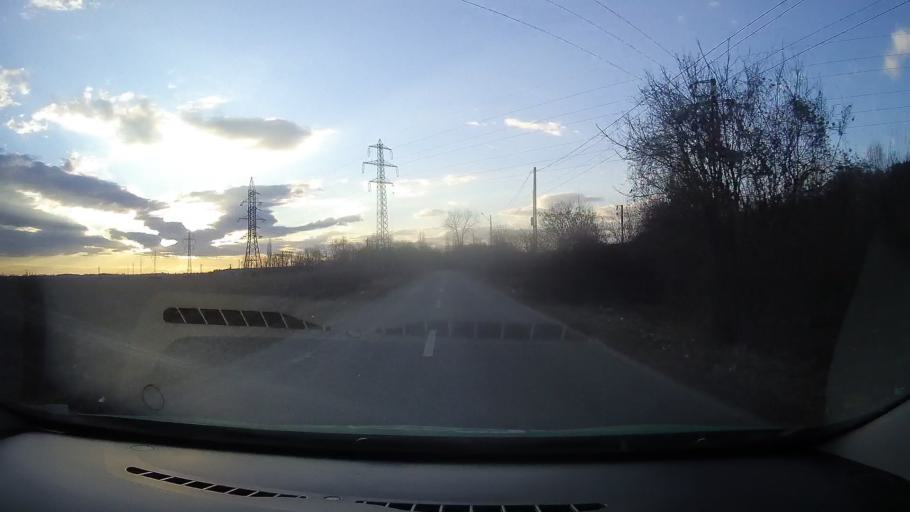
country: RO
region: Dambovita
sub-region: Comuna Gura Ocnitei
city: Gura Ocnitei
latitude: 44.9361
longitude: 25.5882
